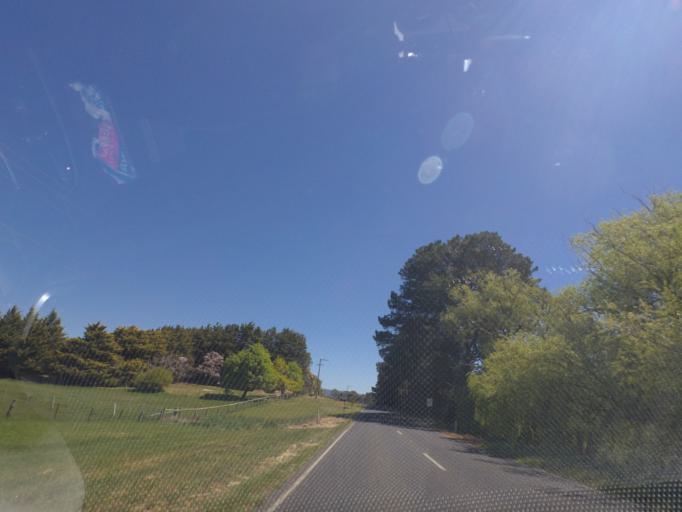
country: AU
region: Victoria
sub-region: Hume
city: Sunbury
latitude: -37.2793
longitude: 144.7477
